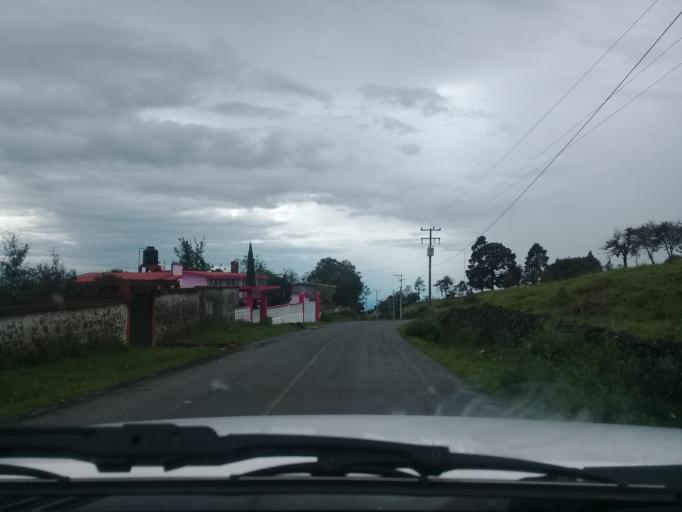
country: MX
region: Veracruz
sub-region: Acajete
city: La Joya
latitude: 19.6152
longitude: -97.0099
